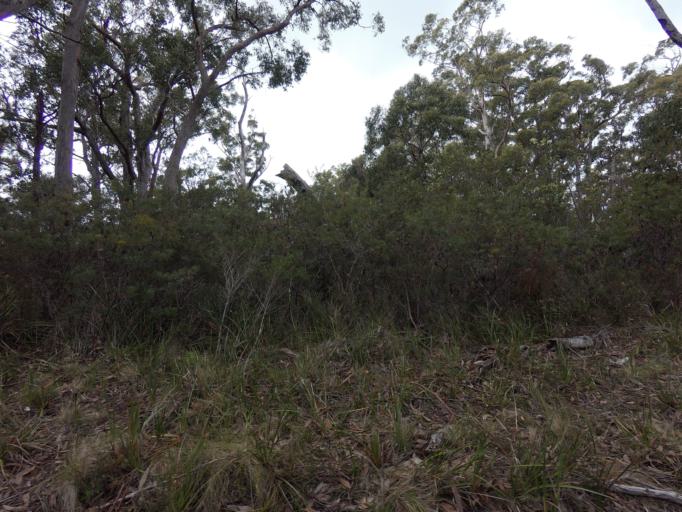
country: AU
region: Tasmania
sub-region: Huon Valley
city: Geeveston
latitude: -43.4688
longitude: 146.9320
